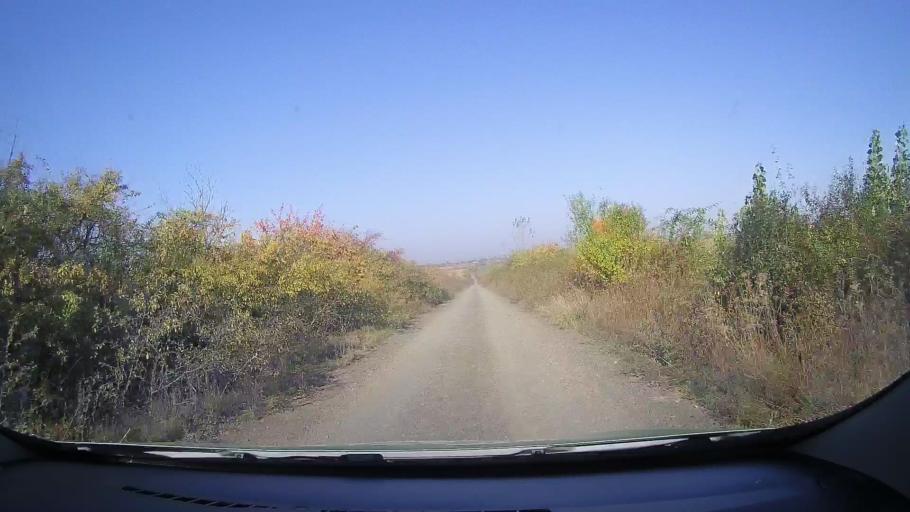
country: RO
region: Satu Mare
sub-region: Comuna Sauca
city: Sauca
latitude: 47.4776
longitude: 22.4746
